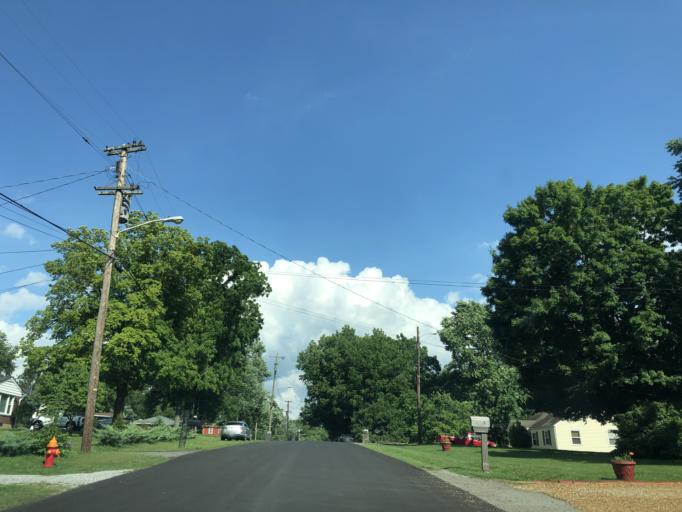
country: US
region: Tennessee
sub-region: Davidson County
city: Nashville
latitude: 36.2109
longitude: -86.7639
